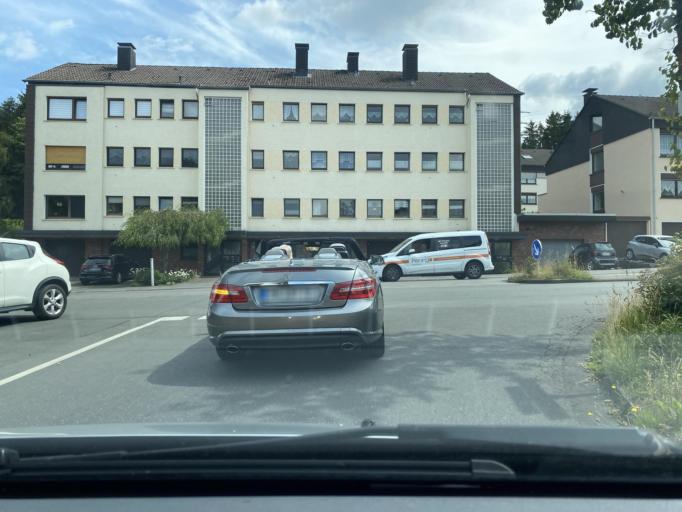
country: DE
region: North Rhine-Westphalia
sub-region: Regierungsbezirk Arnsberg
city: Luedenscheid
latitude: 51.2400
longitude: 7.6119
